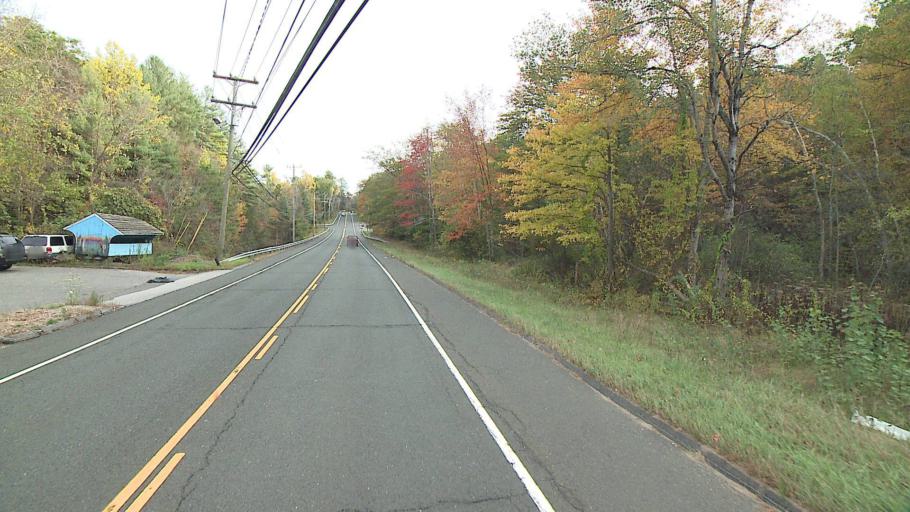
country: US
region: Connecticut
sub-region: Litchfield County
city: New Hartford Center
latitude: 41.9033
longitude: -72.9963
